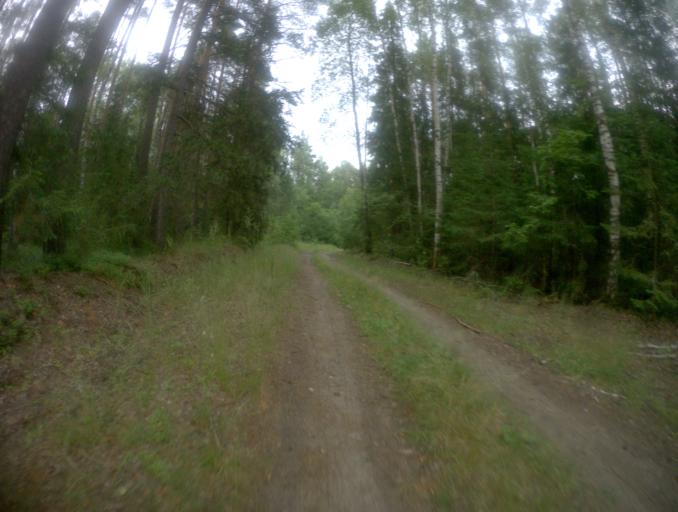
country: RU
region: Ivanovo
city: Talitsy
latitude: 56.6061
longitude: 42.4523
